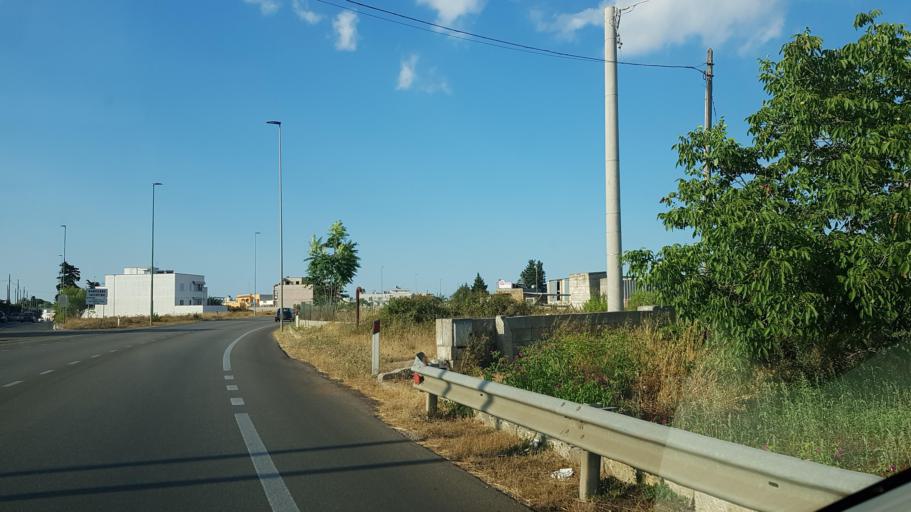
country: IT
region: Apulia
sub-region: Provincia di Lecce
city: Montesano Salentino
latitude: 39.9678
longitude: 18.3232
